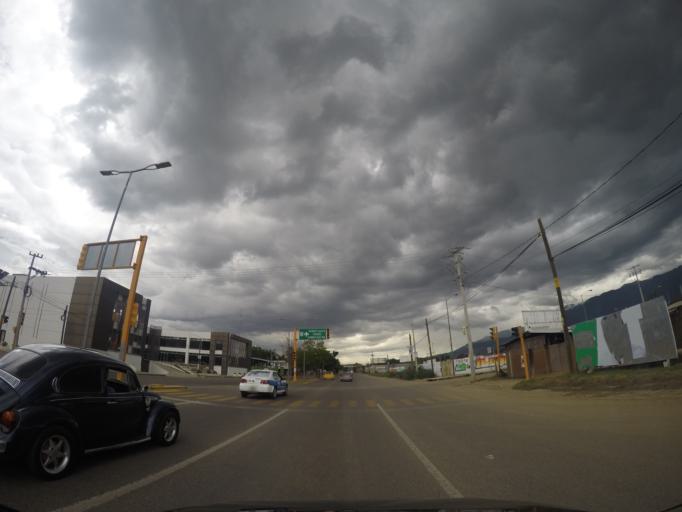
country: MX
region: Oaxaca
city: Tlalixtac de Cabrera
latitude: 17.0544
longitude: -96.6515
